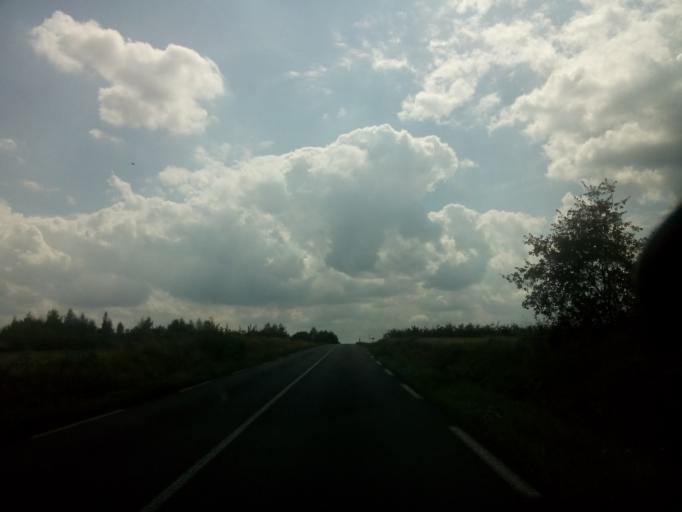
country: FR
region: Centre
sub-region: Departement d'Indre-et-Loire
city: Cheille
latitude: 47.2901
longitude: 0.4213
